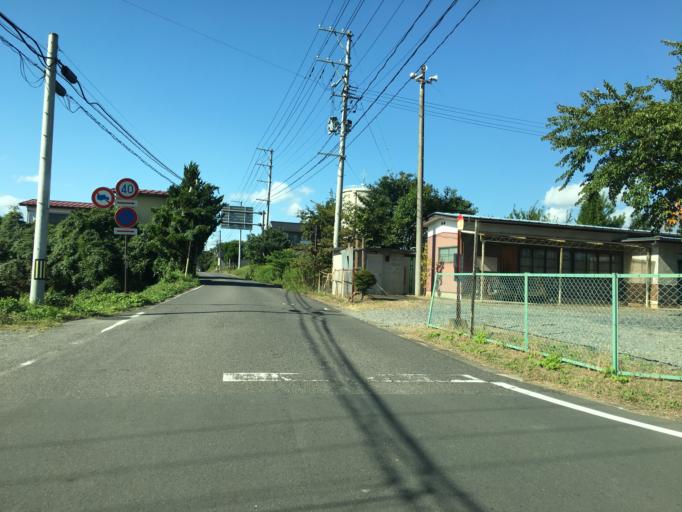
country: JP
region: Fukushima
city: Sukagawa
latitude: 37.2697
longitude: 140.3813
